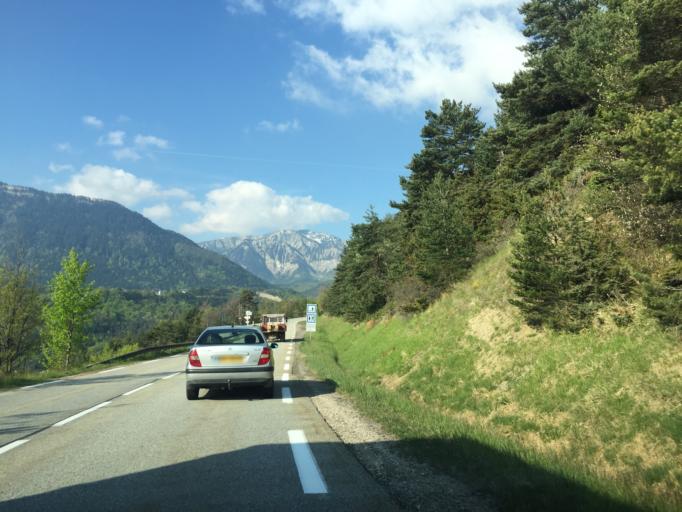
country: FR
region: Rhone-Alpes
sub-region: Departement de l'Isere
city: Mens
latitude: 44.8415
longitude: 5.6176
